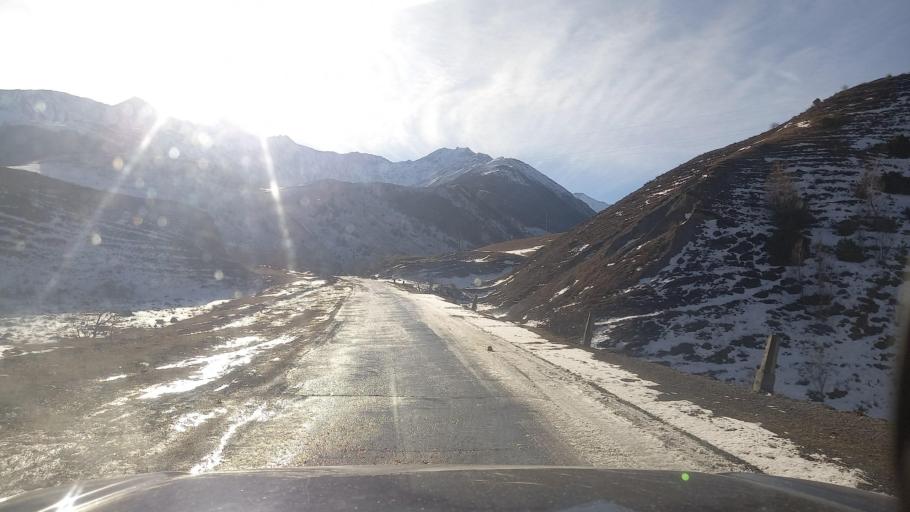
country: RU
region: Ingushetiya
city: Dzhayrakh
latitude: 42.8464
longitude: 44.5152
